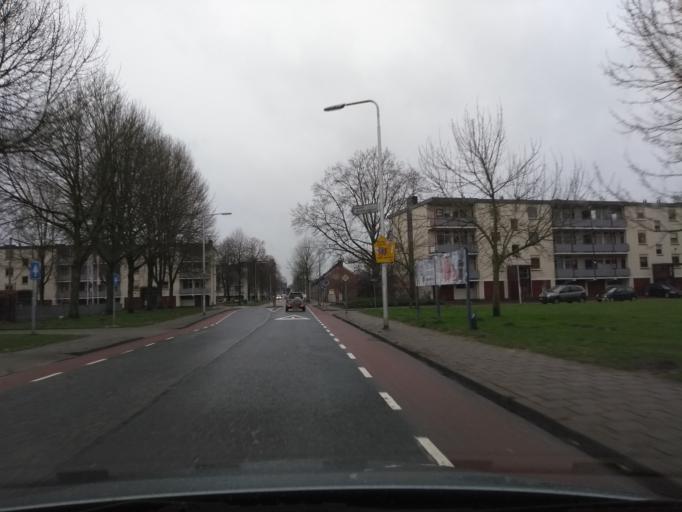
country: NL
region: Overijssel
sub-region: Gemeente Almelo
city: Almelo
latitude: 52.3505
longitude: 6.6452
